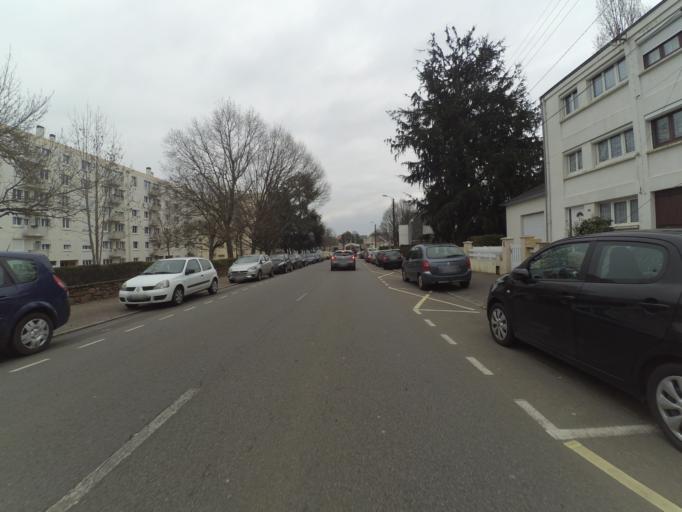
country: FR
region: Pays de la Loire
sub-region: Departement de la Loire-Atlantique
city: Saint-Herblain
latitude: 47.2183
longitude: -1.6054
